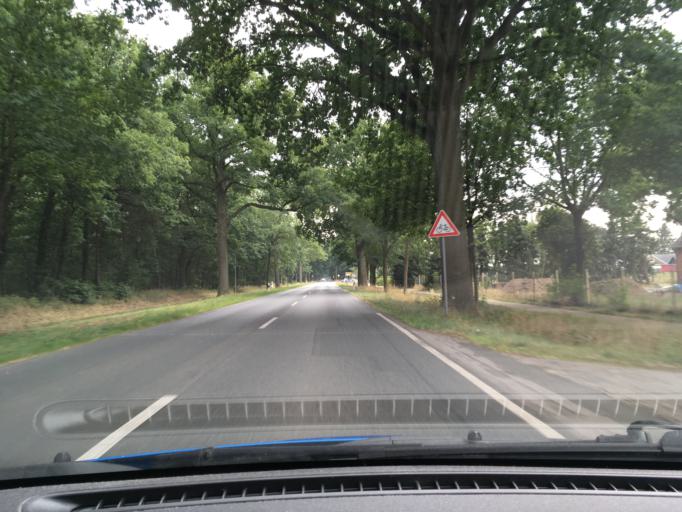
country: DE
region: Lower Saxony
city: Adelheidsdorf
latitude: 52.5551
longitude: 10.0567
